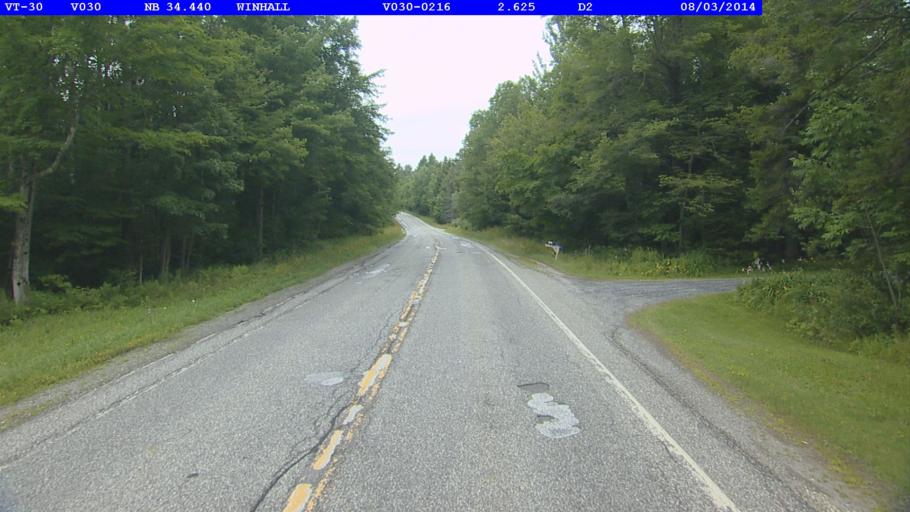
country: US
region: Vermont
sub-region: Bennington County
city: Manchester Center
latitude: 43.1548
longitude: -72.9132
